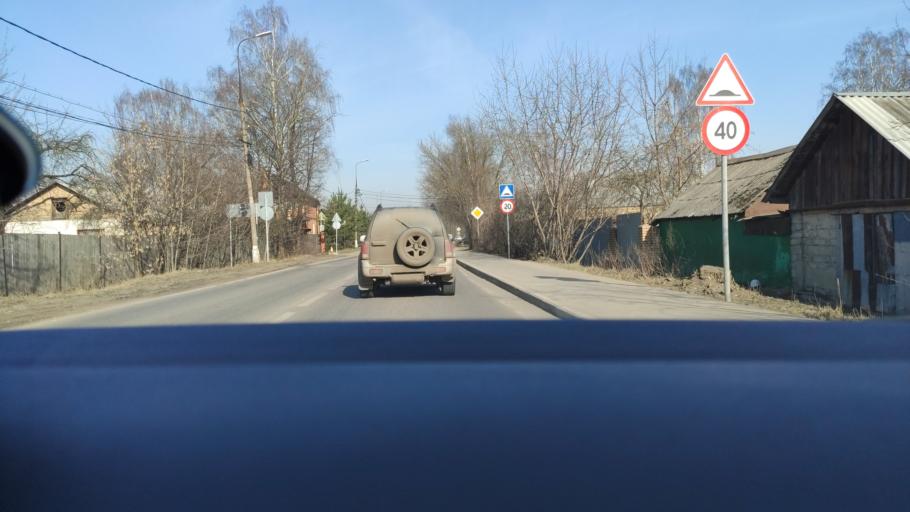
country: RU
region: Moskovskaya
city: Staraya Kupavna
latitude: 55.8134
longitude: 38.1844
